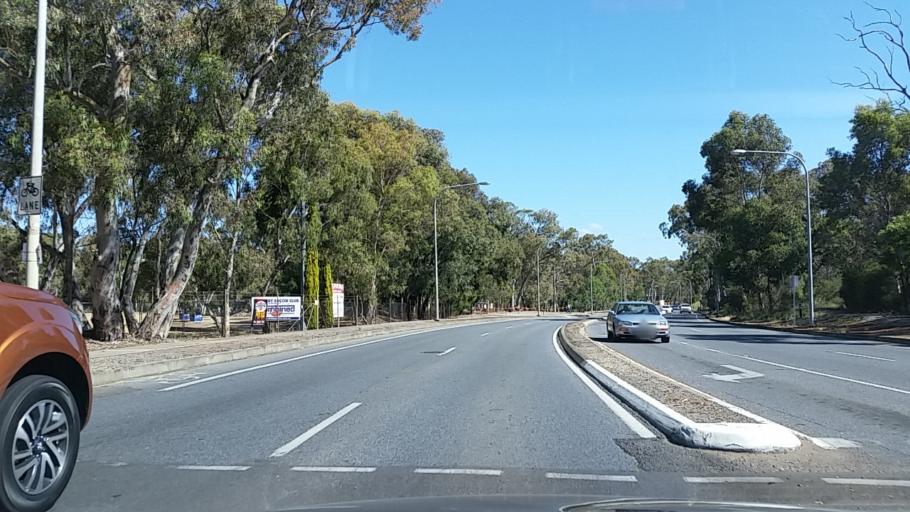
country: AU
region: South Australia
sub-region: Tea Tree Gully
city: Hope Valley
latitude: -34.8175
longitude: 138.6949
